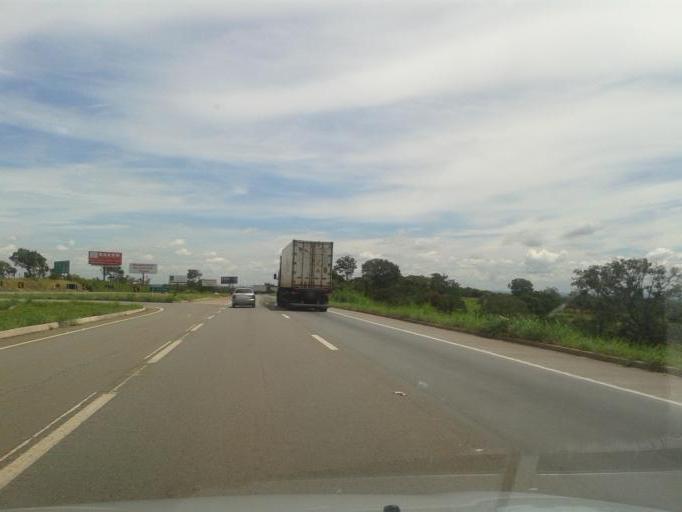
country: BR
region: Goias
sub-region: Hidrolandia
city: Hidrolandia
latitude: -16.9186
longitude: -49.2528
